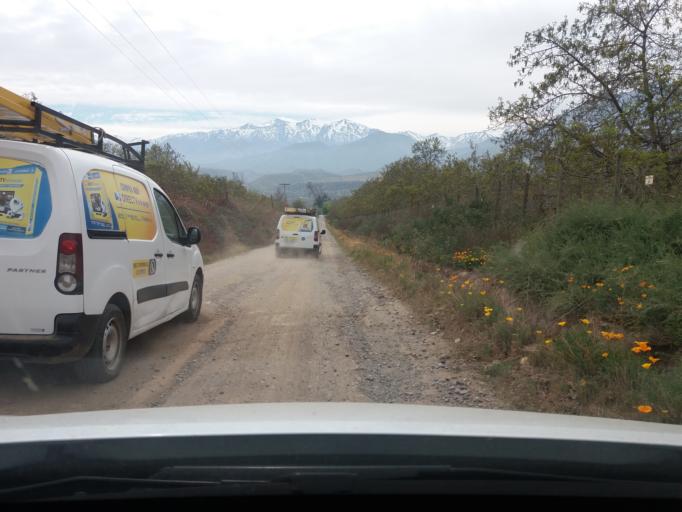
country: CL
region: Valparaiso
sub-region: Provincia de Los Andes
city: Los Andes
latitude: -32.8429
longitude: -70.5520
